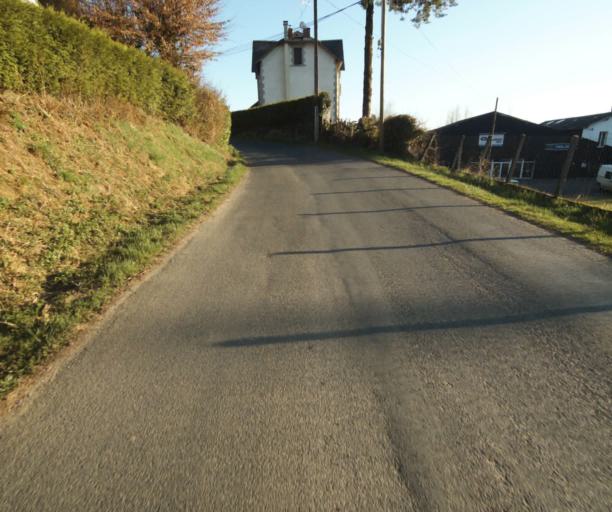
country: FR
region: Limousin
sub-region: Departement de la Correze
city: Saint-Clement
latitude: 45.3433
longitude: 1.6710
